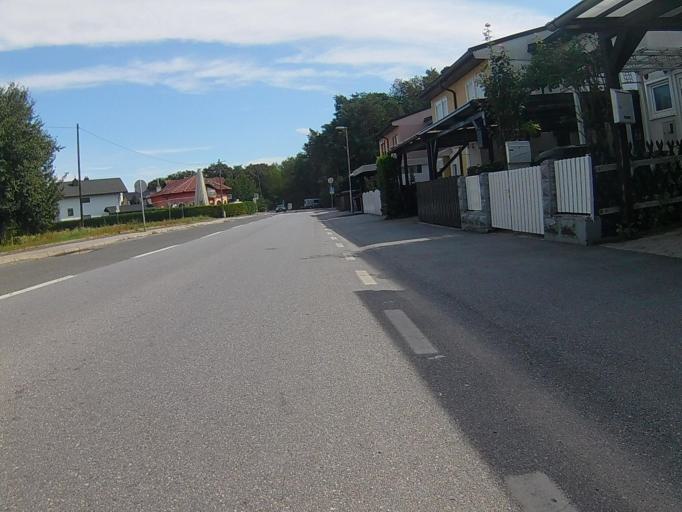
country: SI
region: Miklavz na Dravskem Polju
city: Miklavz na Dravskem Polju
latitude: 46.5268
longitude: 15.6867
